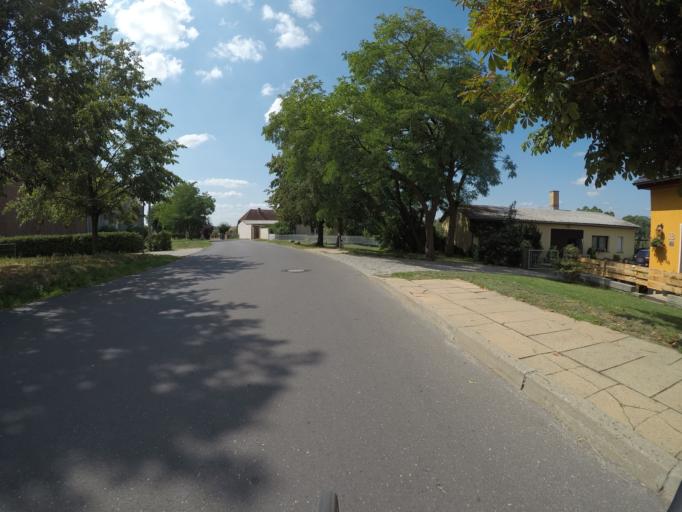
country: DE
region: Brandenburg
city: Werder
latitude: 52.4068
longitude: 12.9603
